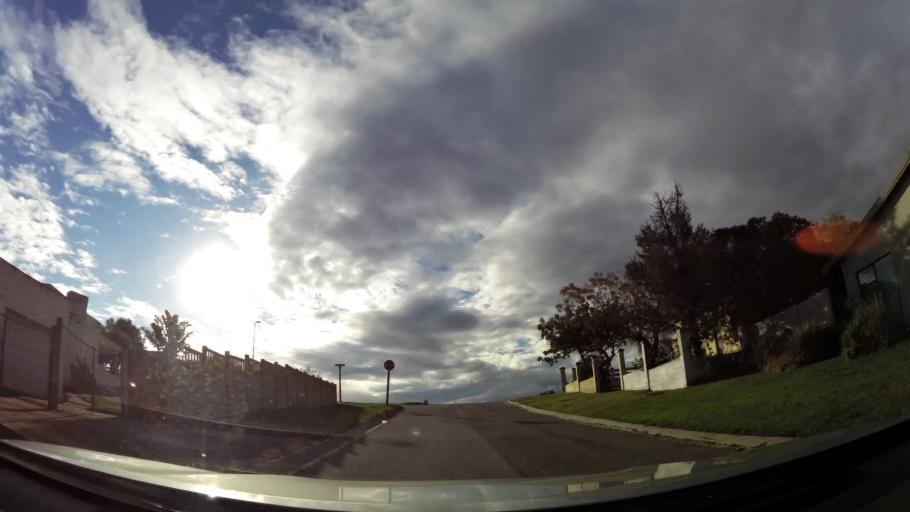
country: ZA
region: Eastern Cape
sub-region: Nelson Mandela Bay Metropolitan Municipality
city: Port Elizabeth
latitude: -33.9487
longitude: 25.4803
